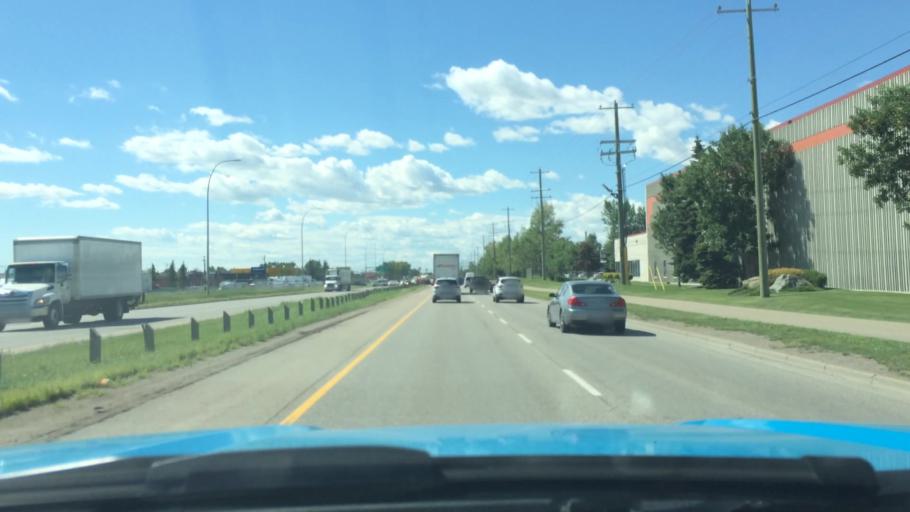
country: CA
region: Alberta
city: Calgary
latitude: 51.0064
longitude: -113.9587
